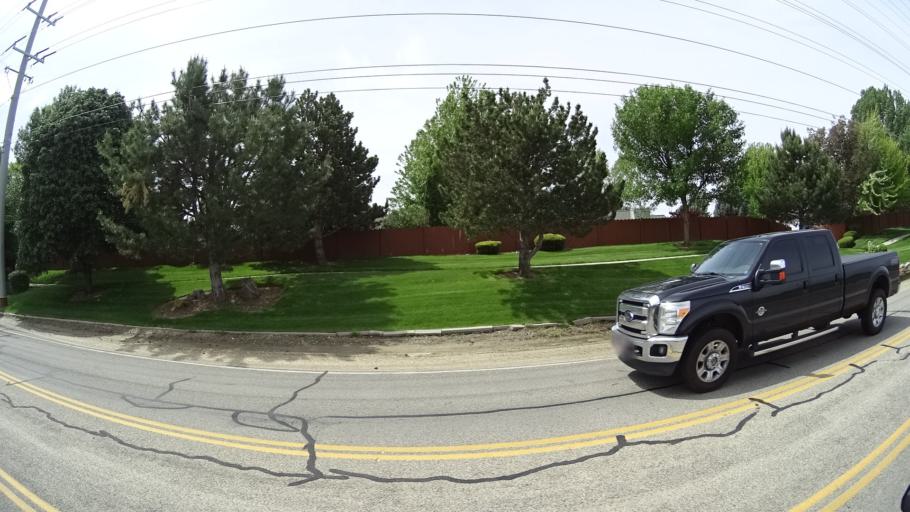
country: US
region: Idaho
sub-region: Ada County
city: Meridian
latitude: 43.5612
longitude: -116.3383
